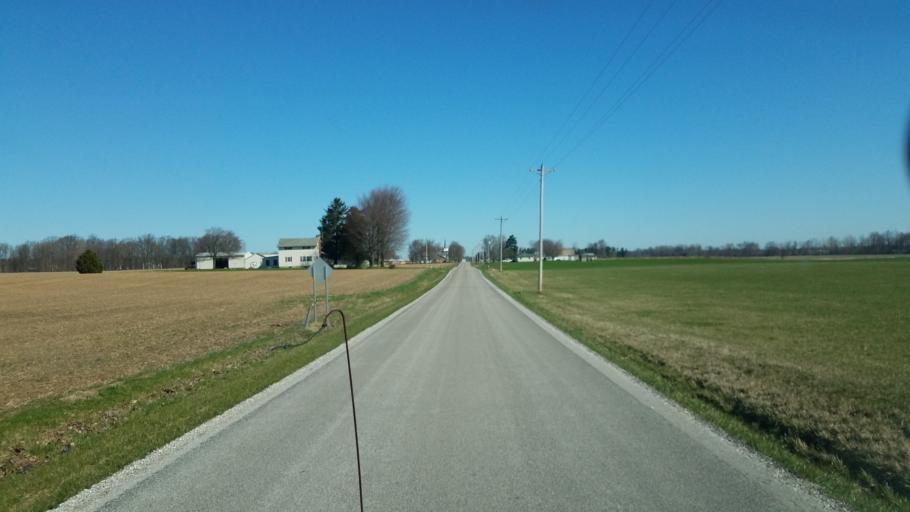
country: US
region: Ohio
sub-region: Huron County
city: Willard
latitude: 40.9617
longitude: -82.7911
